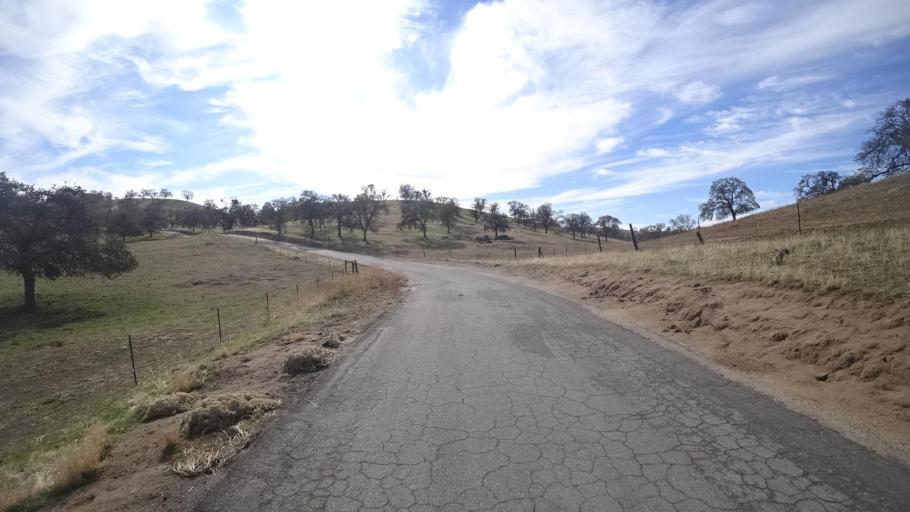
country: US
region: California
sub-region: Kern County
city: Oildale
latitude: 35.6120
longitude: -118.8393
